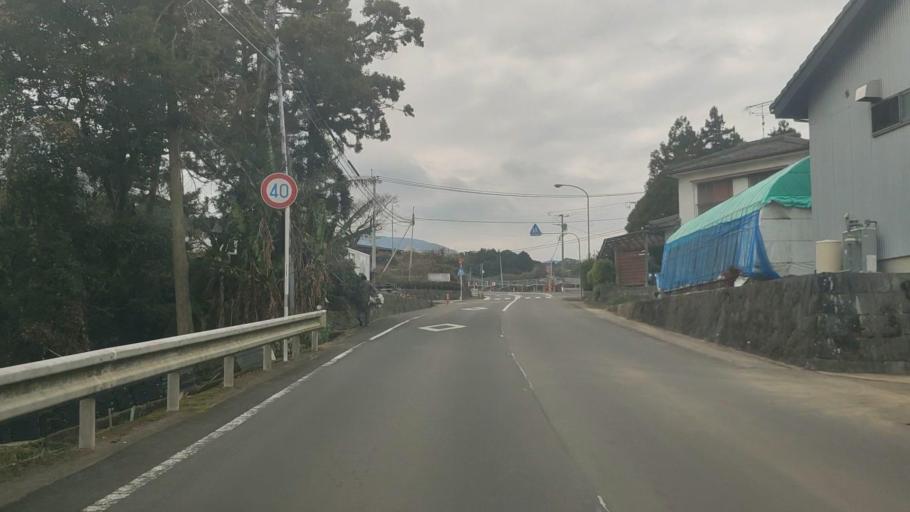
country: JP
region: Nagasaki
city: Shimabara
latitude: 32.8355
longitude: 130.2923
